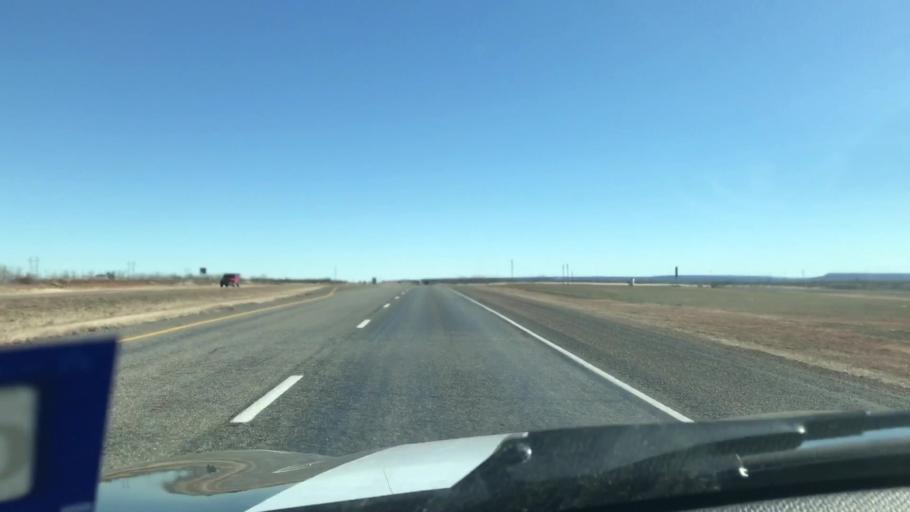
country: US
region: Texas
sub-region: Garza County
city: Post
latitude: 33.1038
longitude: -101.2622
